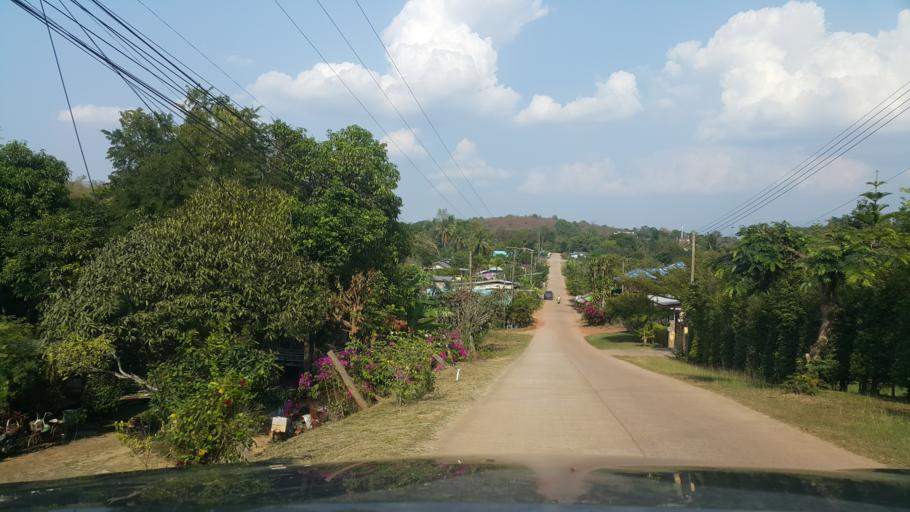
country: TH
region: Phitsanulok
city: Nakhon Thai
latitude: 16.8839
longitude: 100.8397
